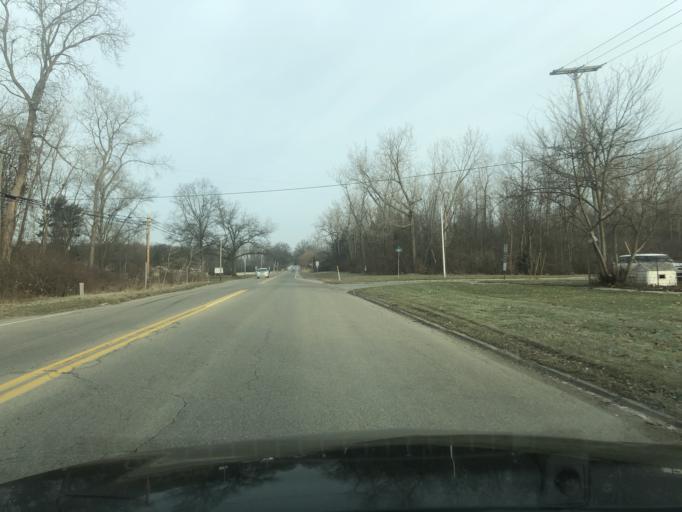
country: US
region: Michigan
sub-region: Wayne County
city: Taylor
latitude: 42.1878
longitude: -83.3257
